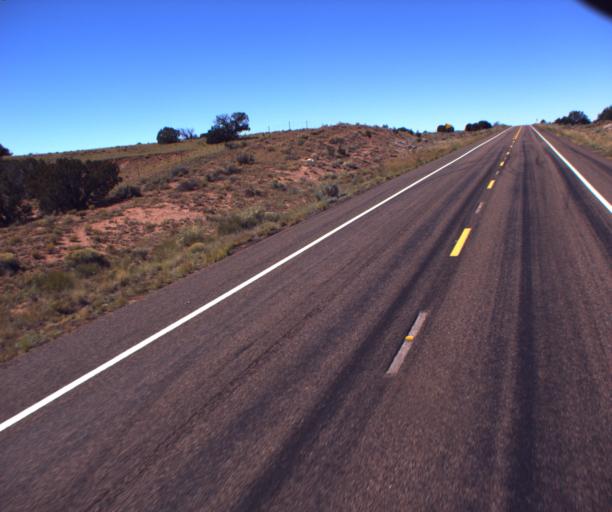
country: US
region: Arizona
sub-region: Apache County
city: Saint Johns
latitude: 34.5941
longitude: -109.6178
